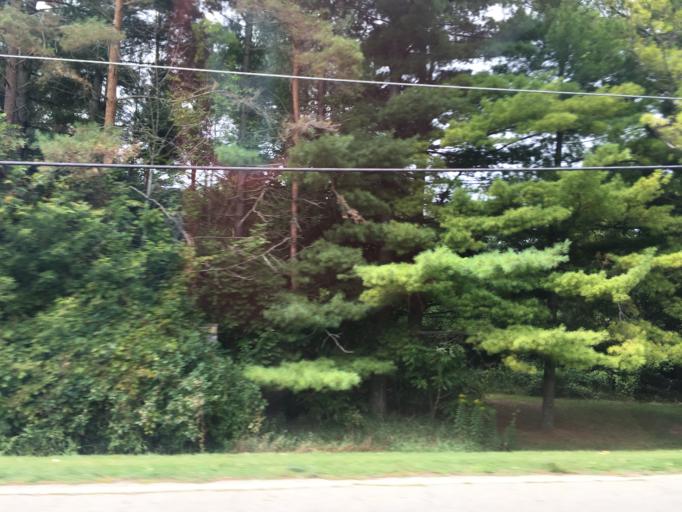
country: US
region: Michigan
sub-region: Lapeer County
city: Barnes Lake-Millers Lake
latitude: 43.3304
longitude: -83.3524
